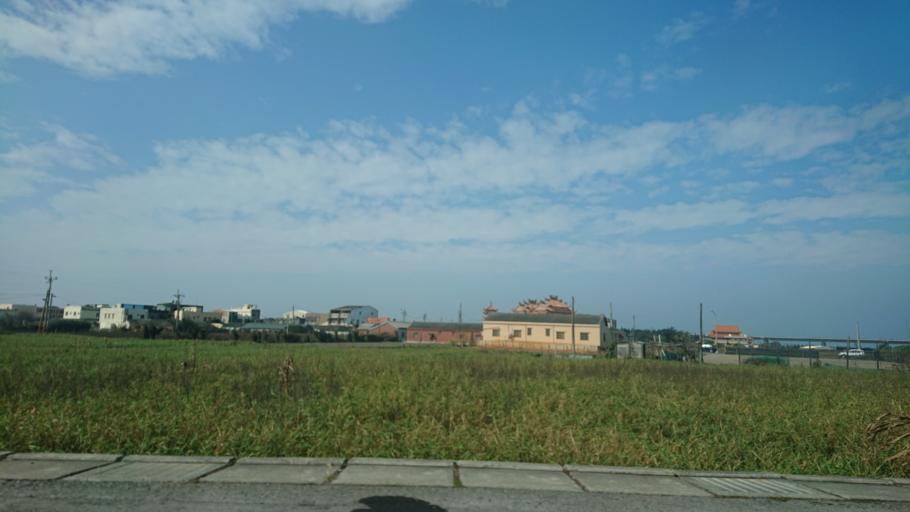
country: TW
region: Taiwan
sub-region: Changhua
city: Chang-hua
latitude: 23.9294
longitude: 120.3219
